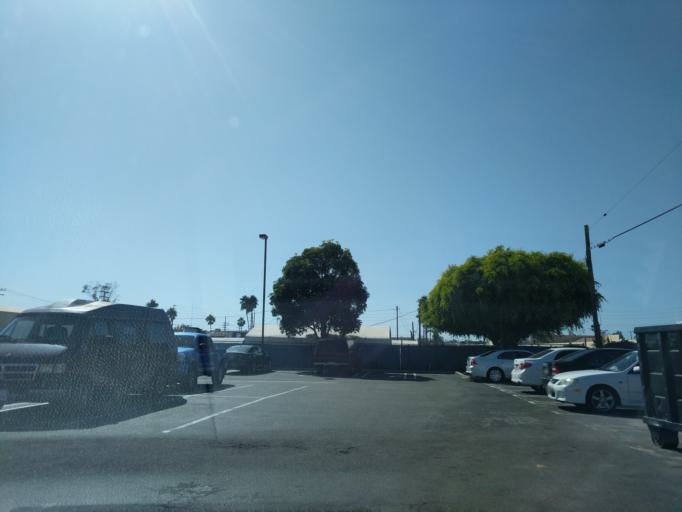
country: US
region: California
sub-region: Orange County
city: Costa Mesa
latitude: 33.6370
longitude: -117.9250
